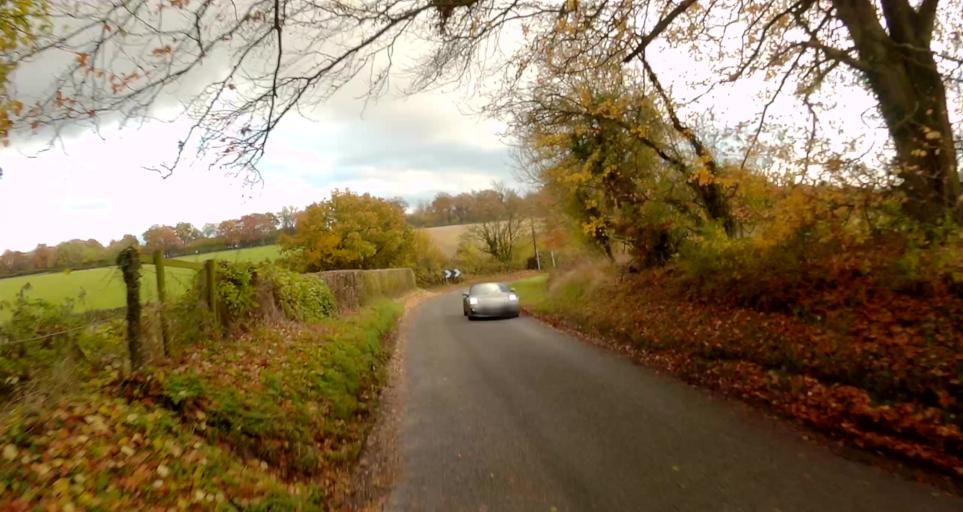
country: GB
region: England
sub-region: Hampshire
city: Old Basing
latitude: 51.2370
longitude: -1.0302
